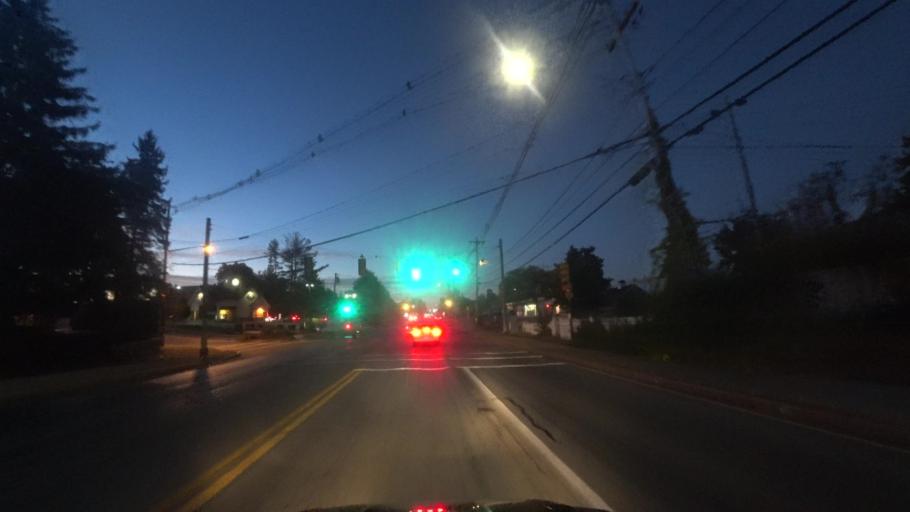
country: US
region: Massachusetts
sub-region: Middlesex County
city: North Reading
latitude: 42.5785
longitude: -71.1116
